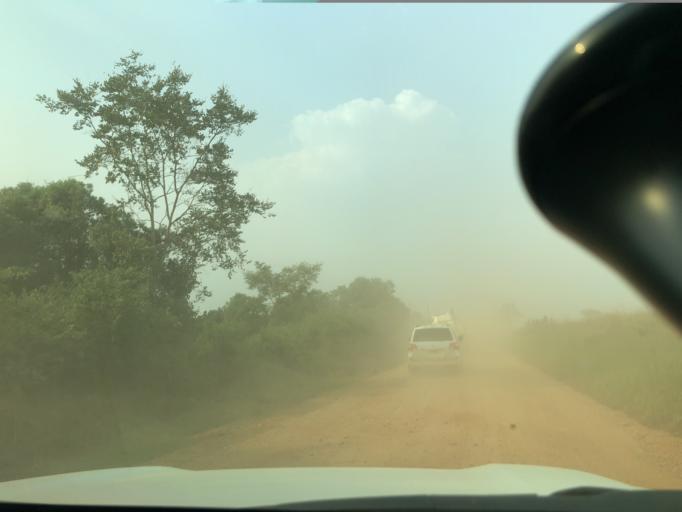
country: CD
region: Nord Kivu
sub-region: North Kivu
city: Butembo
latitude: 0.0968
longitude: 29.6402
